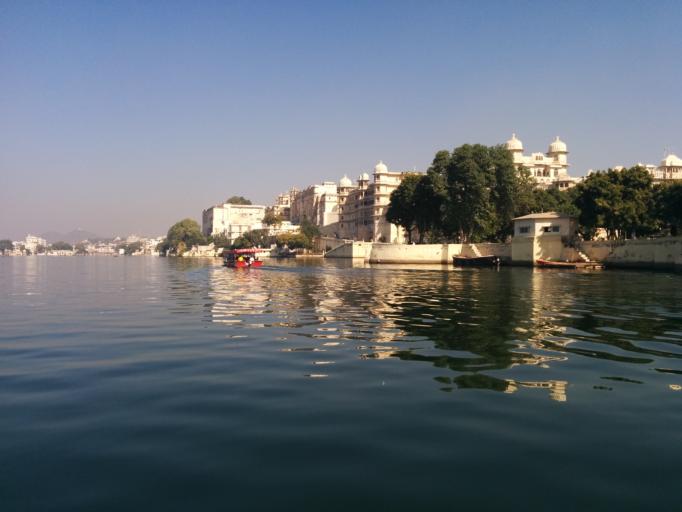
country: IN
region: Rajasthan
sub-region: Udaipur
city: Udaipur
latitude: 24.5727
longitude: 73.6825
